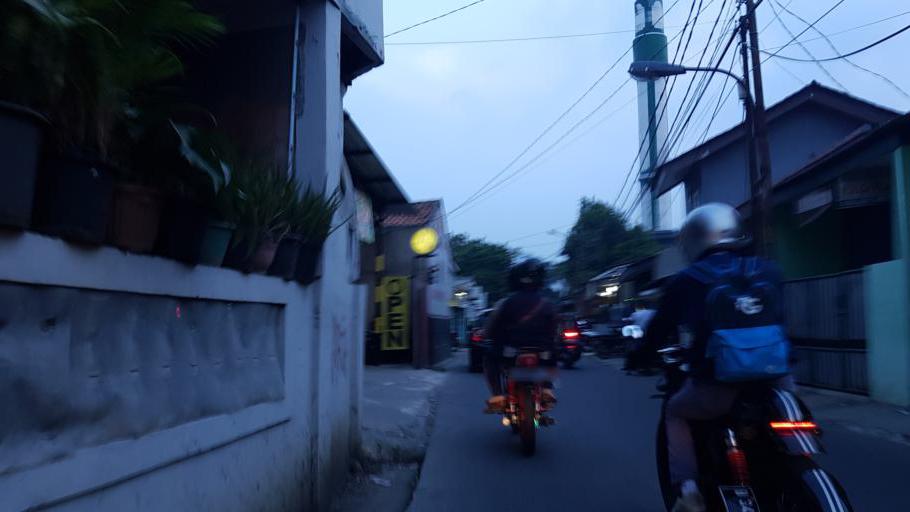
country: ID
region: West Java
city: Pamulang
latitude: -6.3185
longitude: 106.7938
